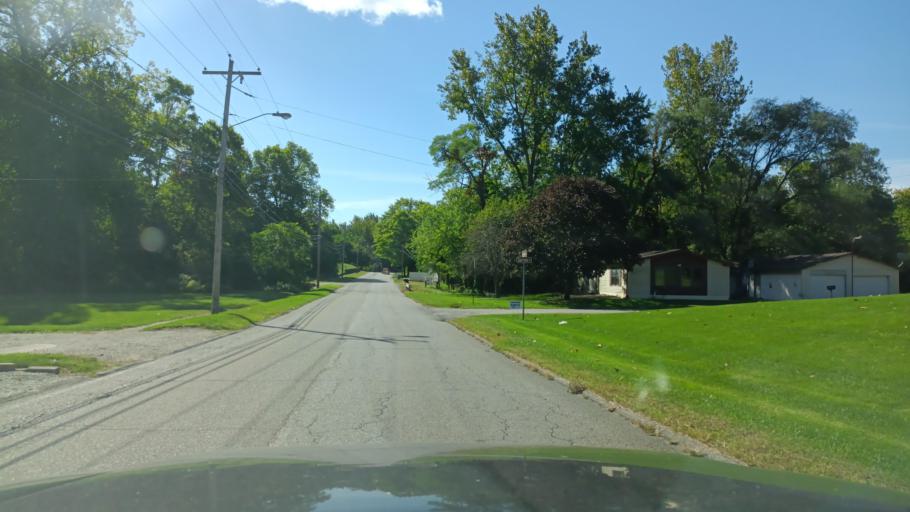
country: US
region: Indiana
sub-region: Fountain County
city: Covington
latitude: 40.1366
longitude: -87.3865
